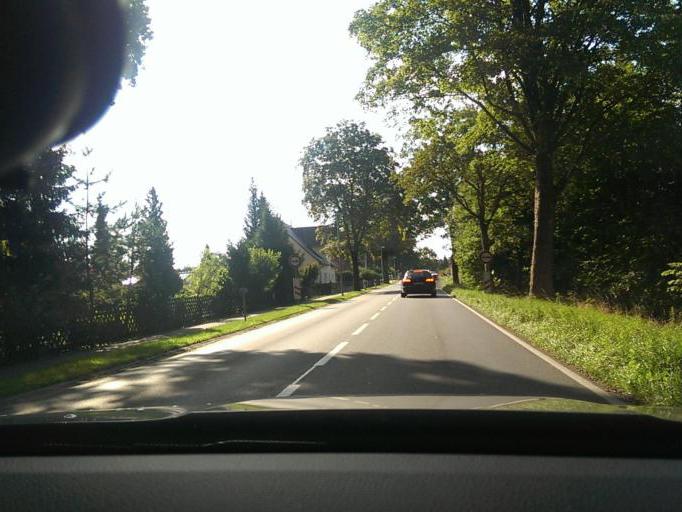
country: DE
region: Lower Saxony
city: Elze
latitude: 52.5353
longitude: 9.7452
